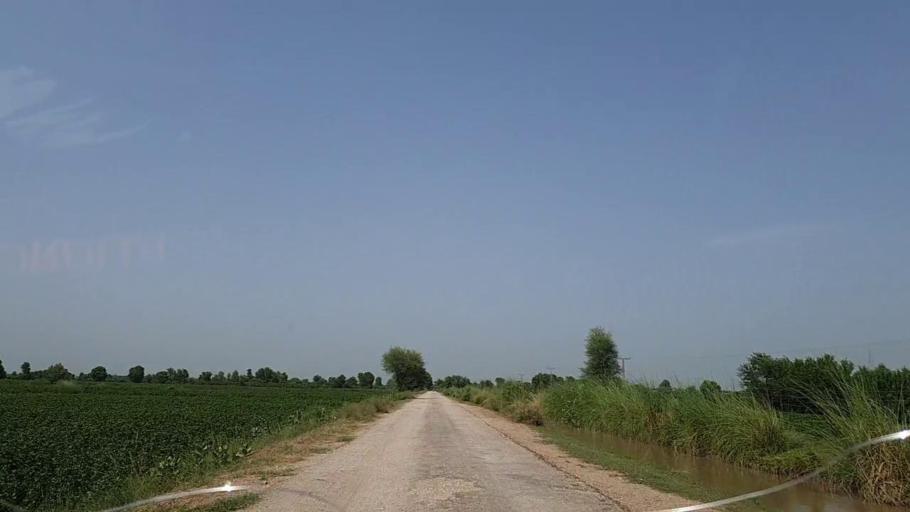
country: PK
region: Sindh
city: Kandiaro
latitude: 27.0350
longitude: 68.1563
